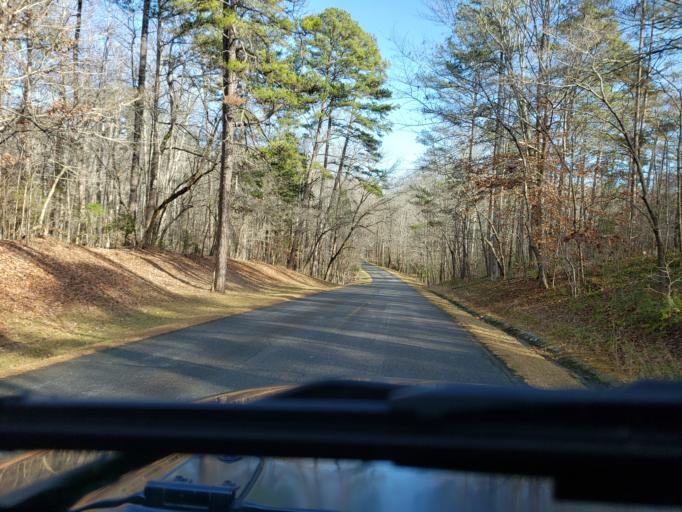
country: US
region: North Carolina
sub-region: Cleveland County
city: White Plains
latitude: 35.1349
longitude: -81.3576
